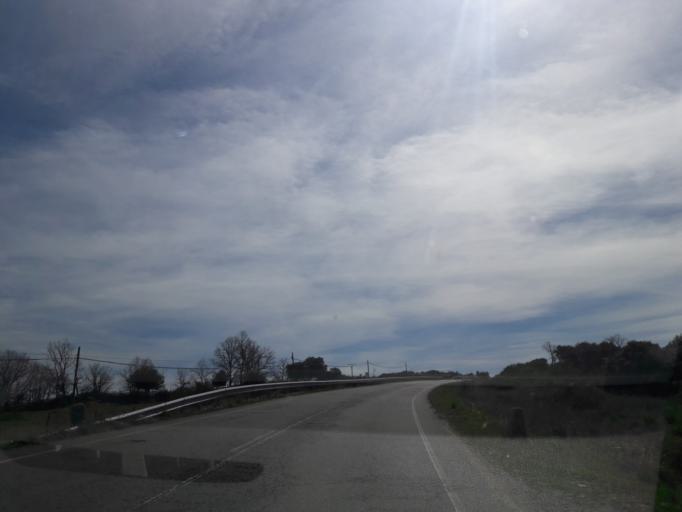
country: ES
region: Castille and Leon
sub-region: Provincia de Salamanca
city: Fuentes de Bejar
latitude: 40.5042
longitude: -5.6878
